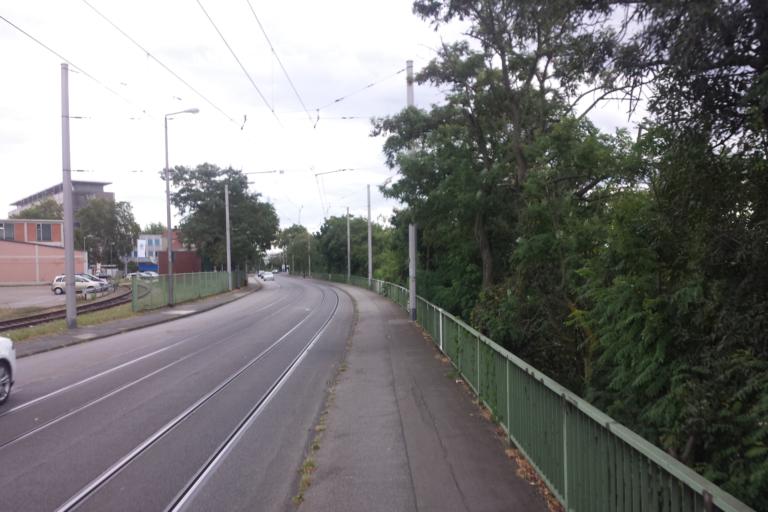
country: DE
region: Baden-Wuerttemberg
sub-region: Karlsruhe Region
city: Mannheim
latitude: 49.5342
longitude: 8.4556
